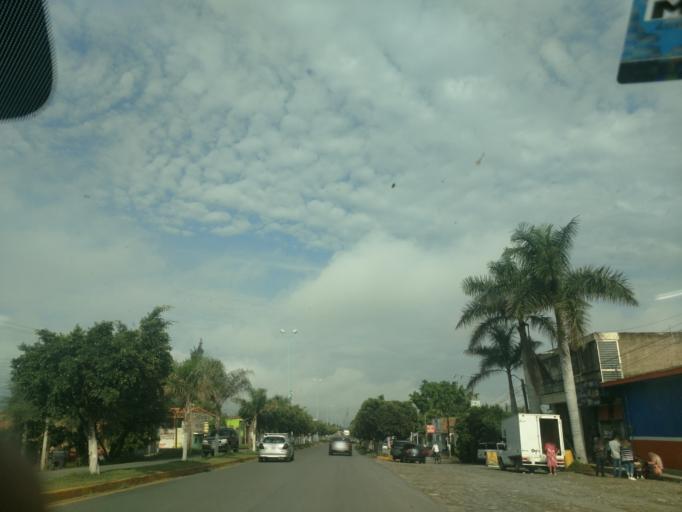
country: MX
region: Jalisco
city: Ameca
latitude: 20.5364
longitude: -104.0329
